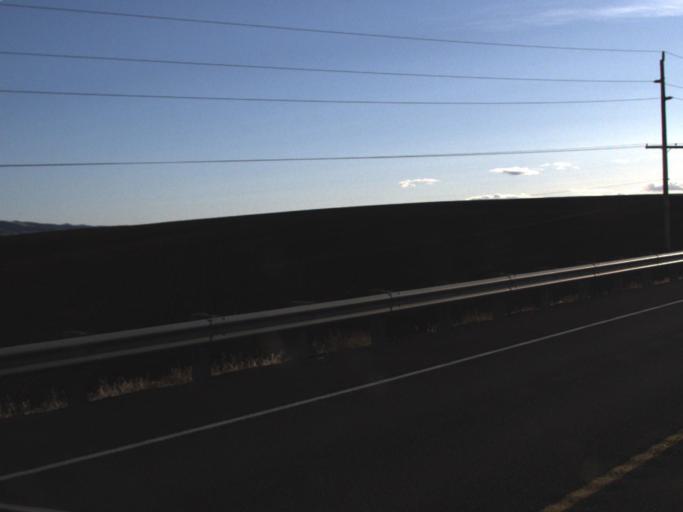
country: US
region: Washington
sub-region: Walla Walla County
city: Walla Walla East
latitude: 46.1125
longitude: -118.2270
